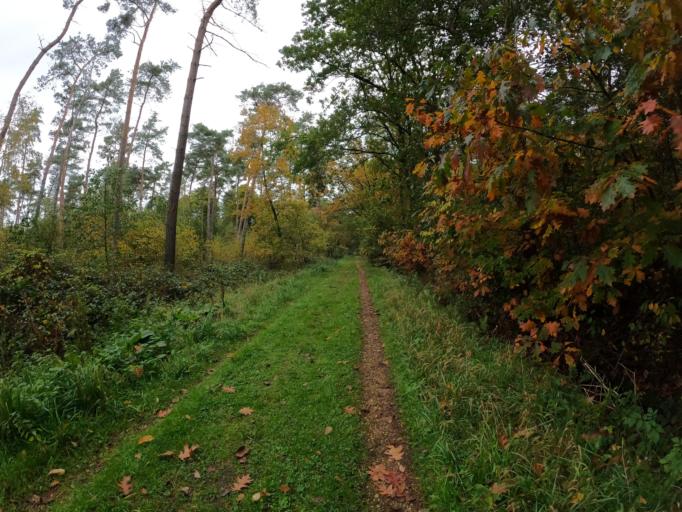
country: BE
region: Flanders
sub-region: Provincie Antwerpen
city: Herenthout
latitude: 51.1390
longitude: 4.7303
